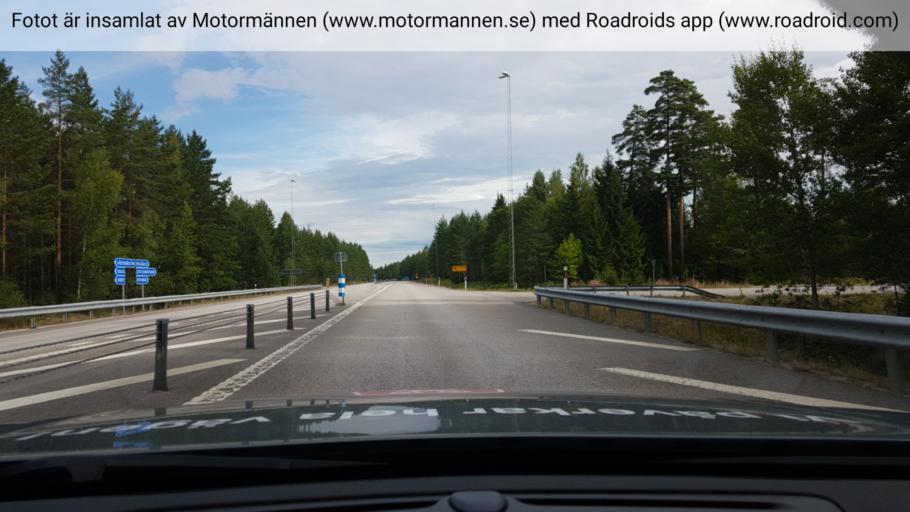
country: SE
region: Uppsala
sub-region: Heby Kommun
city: Tarnsjo
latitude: 60.2342
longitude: 16.9550
